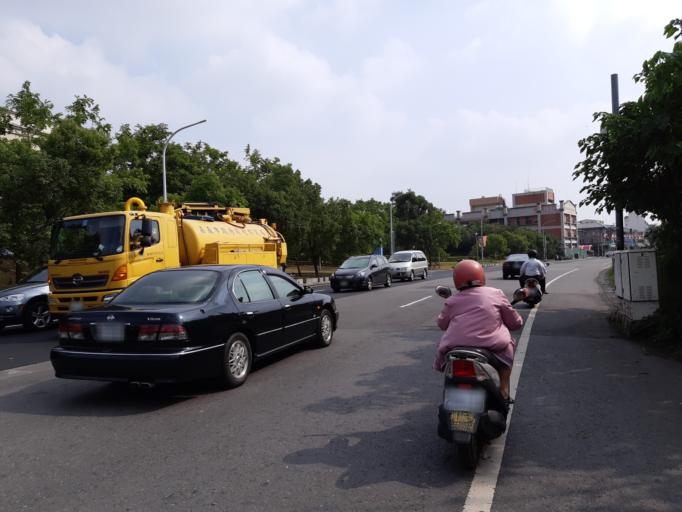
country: TW
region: Taiwan
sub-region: Chiayi
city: Jiayi Shi
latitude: 23.4872
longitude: 120.4602
